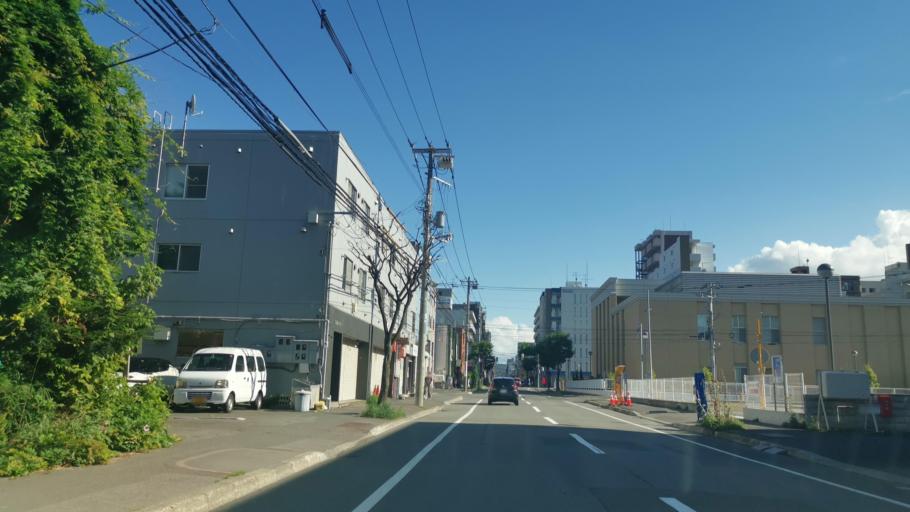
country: JP
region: Hokkaido
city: Sapporo
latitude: 43.0844
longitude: 141.3461
